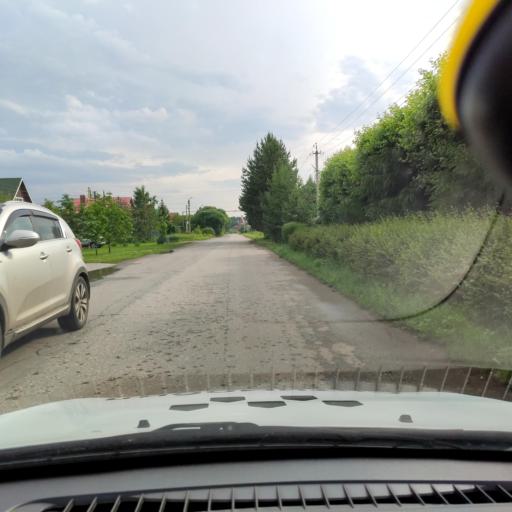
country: RU
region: Samara
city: Podstepki
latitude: 53.5741
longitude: 49.0757
